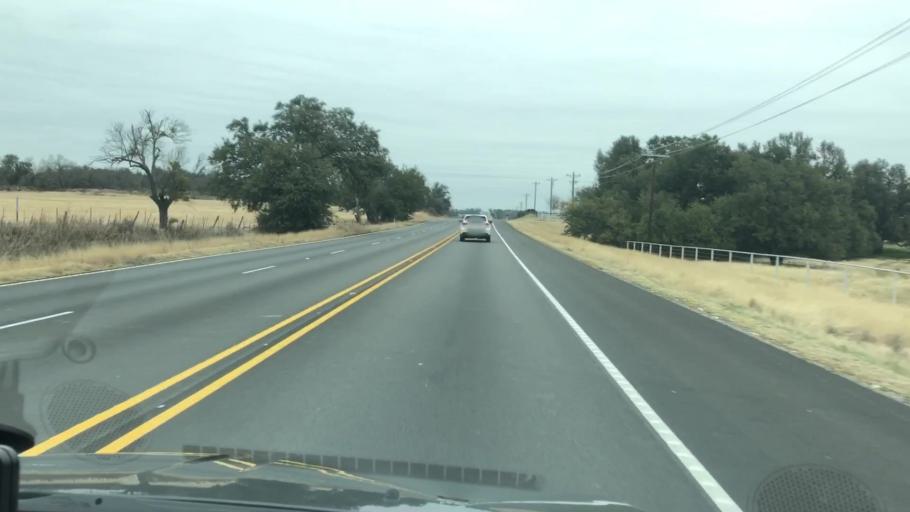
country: US
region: Texas
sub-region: Erath County
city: Stephenville
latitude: 32.3073
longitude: -98.1856
